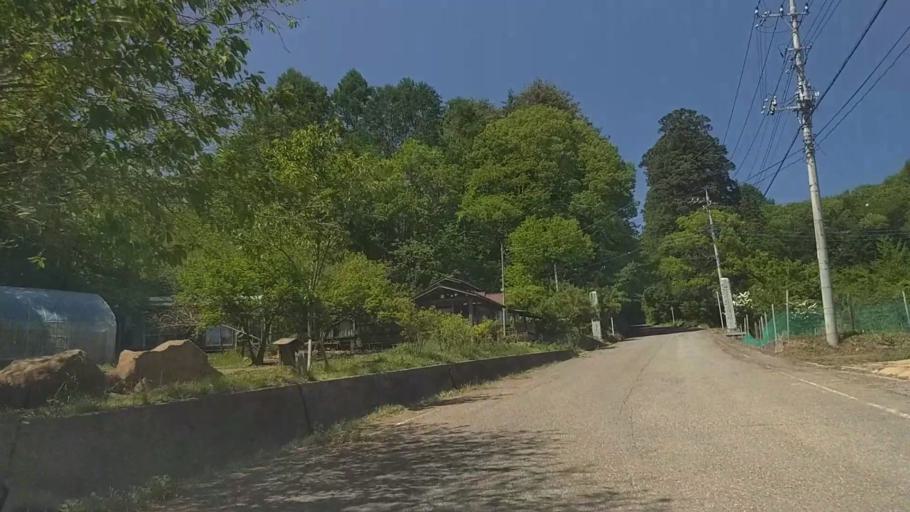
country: JP
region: Yamanashi
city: Nirasaki
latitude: 35.8618
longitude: 138.4468
